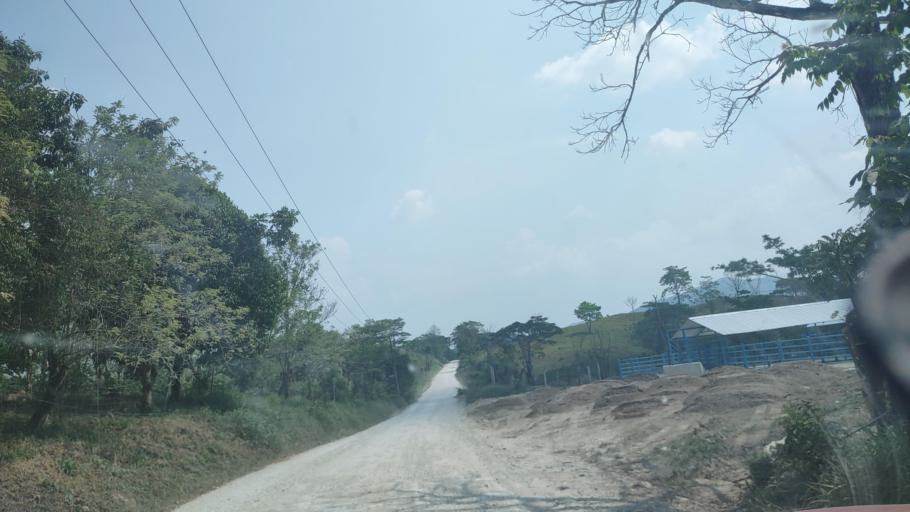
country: MX
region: Tabasco
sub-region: Huimanguillo
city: Francisco Rueda
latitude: 17.5884
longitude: -93.8919
